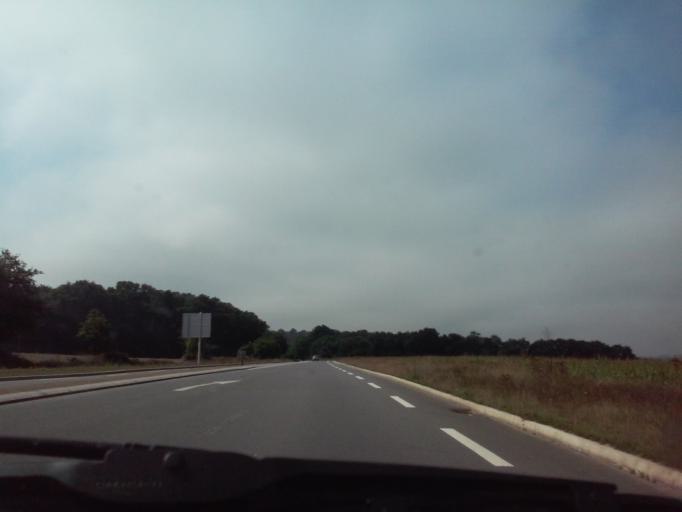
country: FR
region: Brittany
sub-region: Departement du Morbihan
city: Loyat
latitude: 47.9746
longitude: -2.3809
